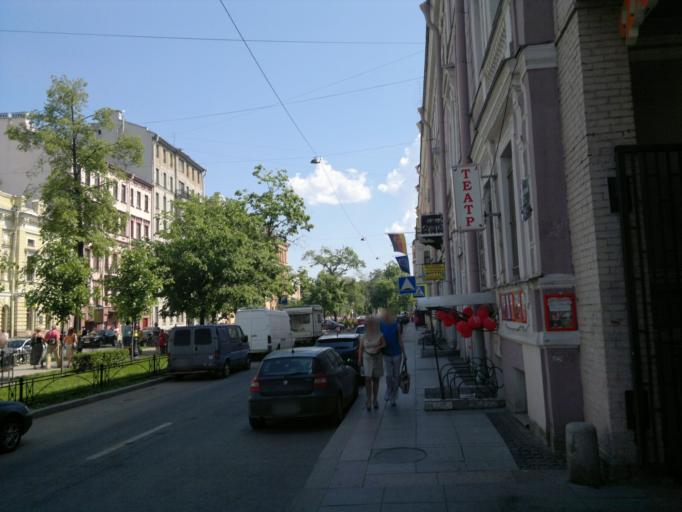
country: RU
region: St.-Petersburg
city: Centralniy
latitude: 59.9450
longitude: 30.3642
